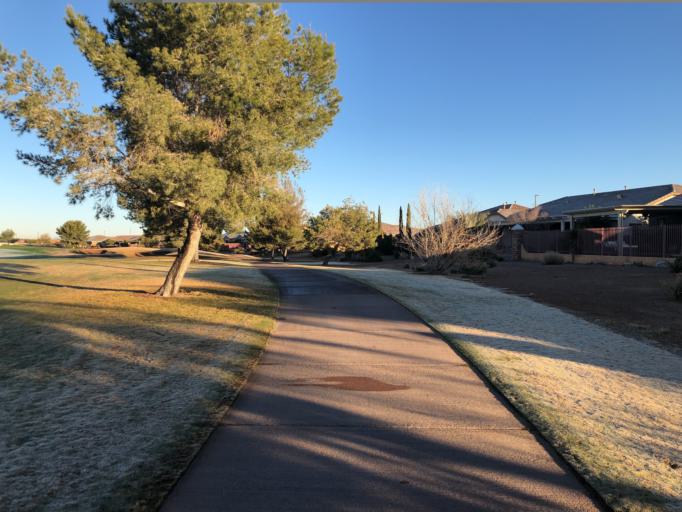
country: US
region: Arizona
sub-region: Maricopa County
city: Queen Creek
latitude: 33.2266
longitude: -111.7095
